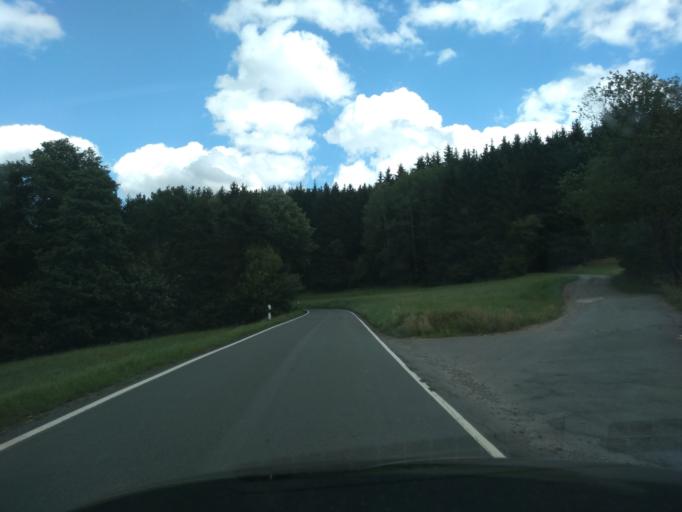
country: DE
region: North Rhine-Westphalia
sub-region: Regierungsbezirk Arnsberg
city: Schalksmuhle
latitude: 51.2315
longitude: 7.5778
